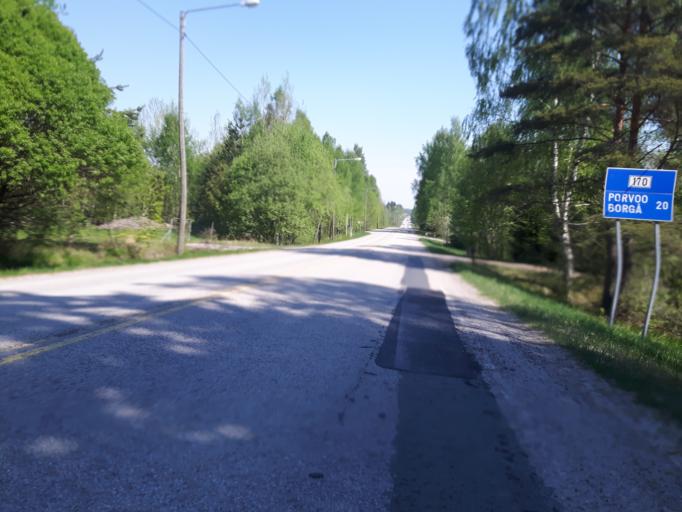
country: FI
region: Uusimaa
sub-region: Helsinki
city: Nickby
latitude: 60.3002
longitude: 25.3619
